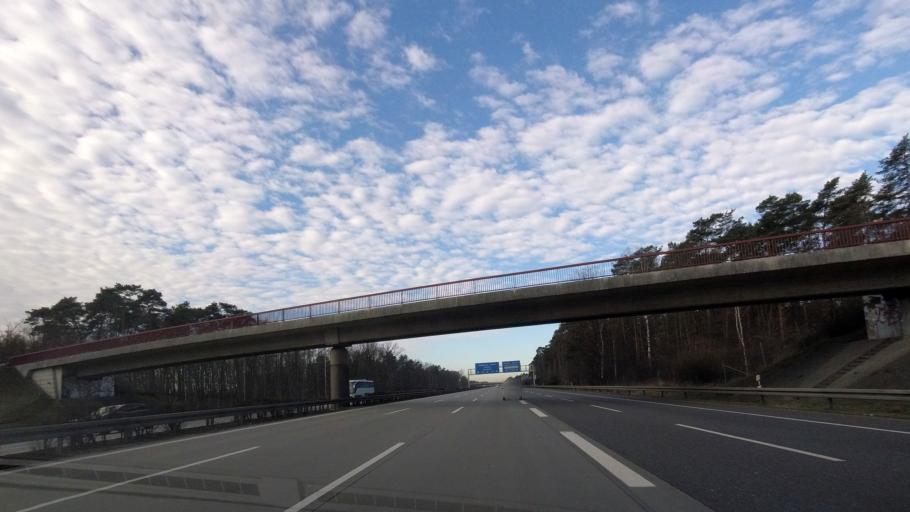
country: DE
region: Brandenburg
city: Schulzendorf
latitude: 52.3173
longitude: 13.5702
